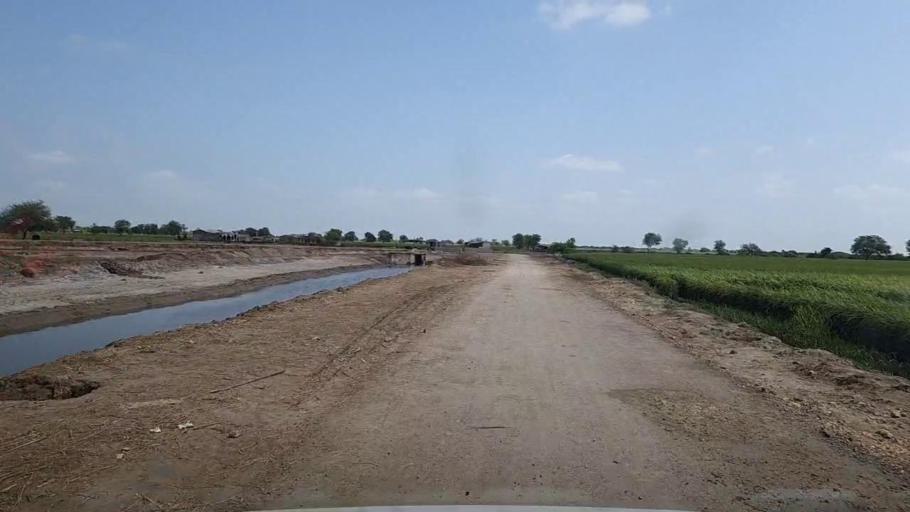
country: PK
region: Sindh
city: Kario
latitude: 24.6813
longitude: 68.5881
